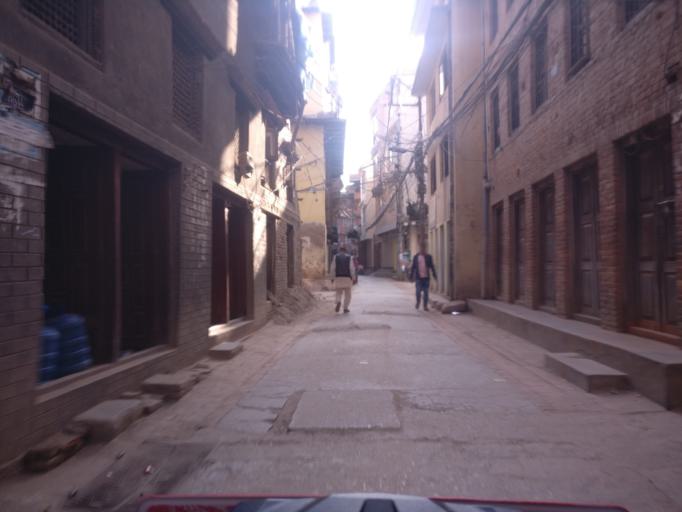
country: NP
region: Central Region
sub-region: Bagmati Zone
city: Patan
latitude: 27.6775
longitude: 85.3249
